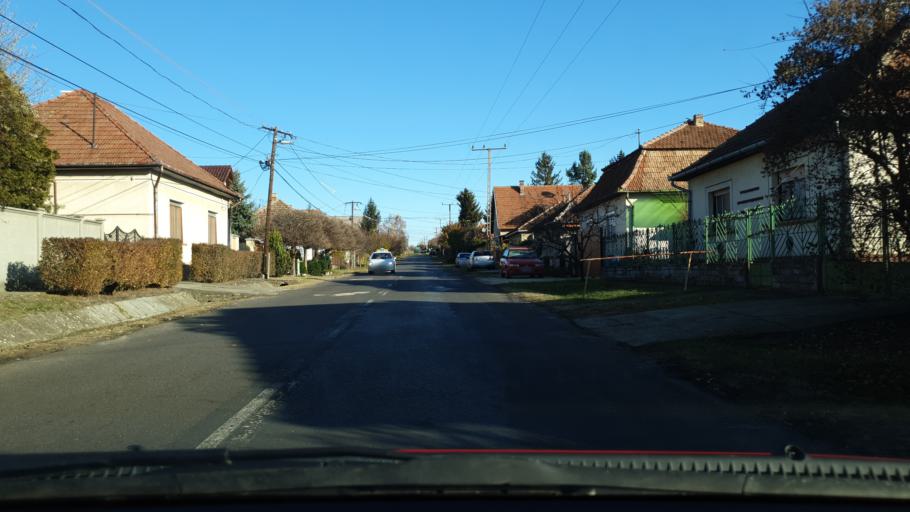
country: HU
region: Pest
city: Cegledbercel
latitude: 47.2147
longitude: 19.6836
